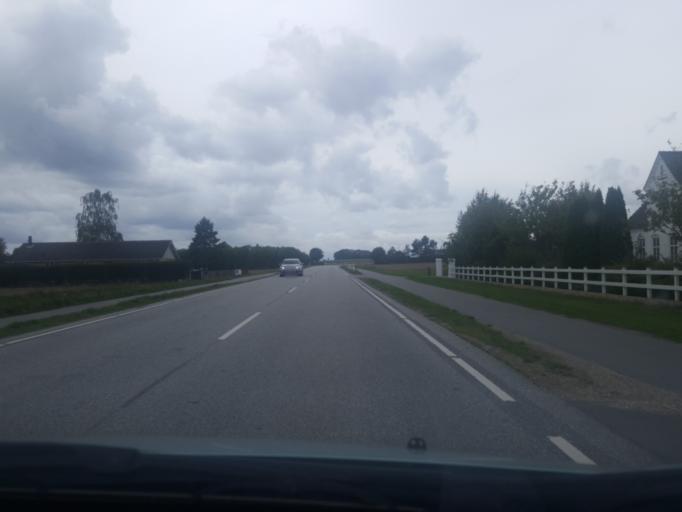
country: DK
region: Zealand
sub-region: Guldborgsund Kommune
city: Nykobing Falster
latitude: 54.7016
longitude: 11.9366
